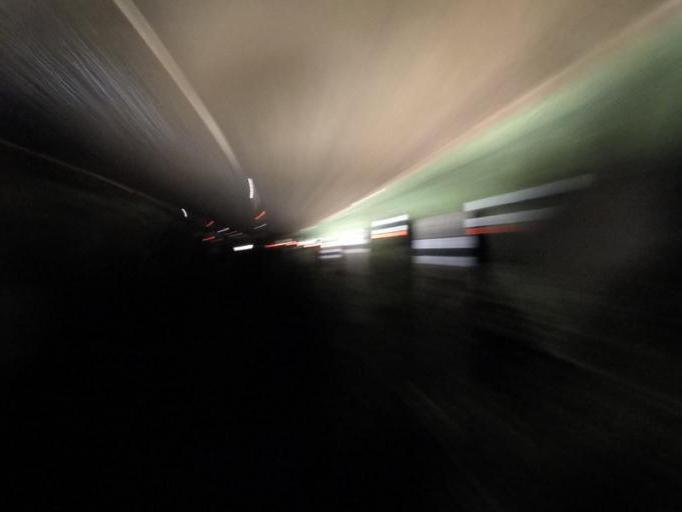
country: IN
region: Tamil Nadu
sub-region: Nilgiri
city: Wellington
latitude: 11.4152
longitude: 76.7930
